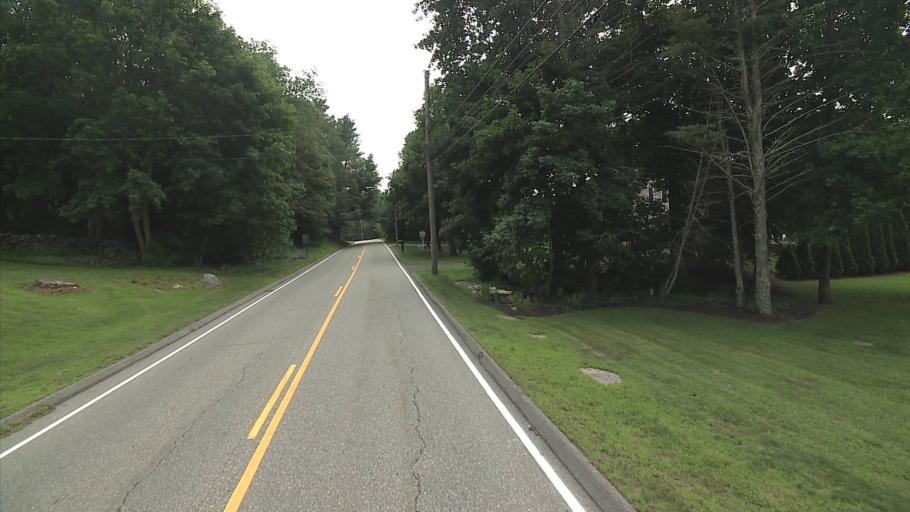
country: US
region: Connecticut
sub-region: Windham County
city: Wauregan
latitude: 41.7775
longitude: -71.9437
